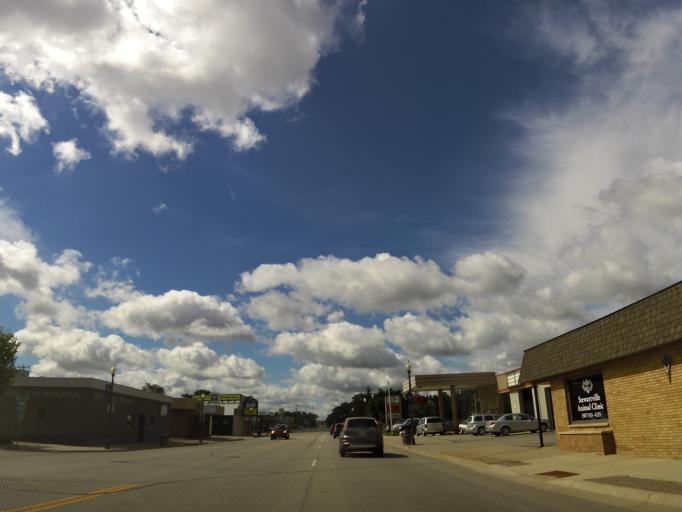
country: US
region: Minnesota
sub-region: Olmsted County
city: Stewartville
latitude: 43.8548
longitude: -92.4886
